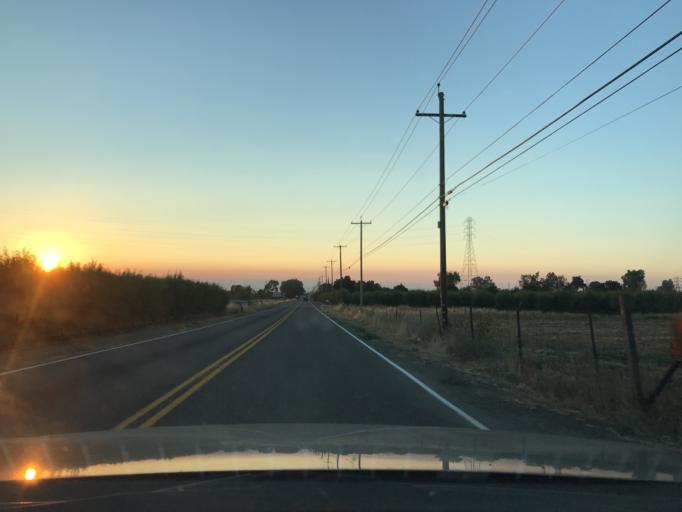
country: US
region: California
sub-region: Merced County
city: Merced
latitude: 37.3391
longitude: -120.5124
